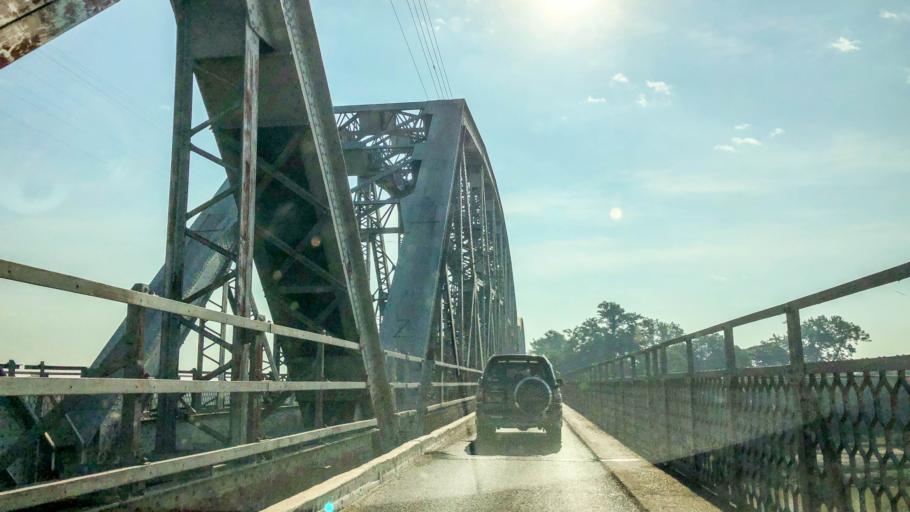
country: MM
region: Sagain
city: Sagaing
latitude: 21.8697
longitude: 95.9940
